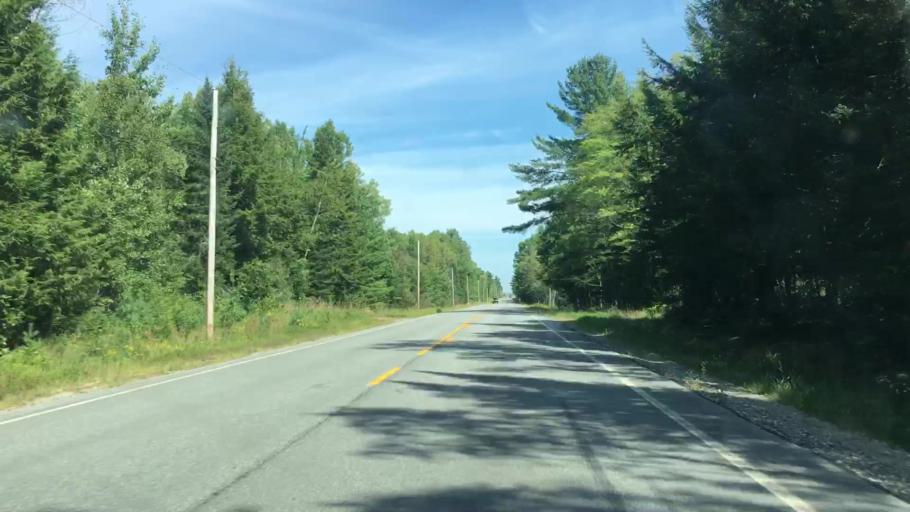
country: US
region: Maine
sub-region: Penobscot County
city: Howland
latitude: 45.2323
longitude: -68.6958
